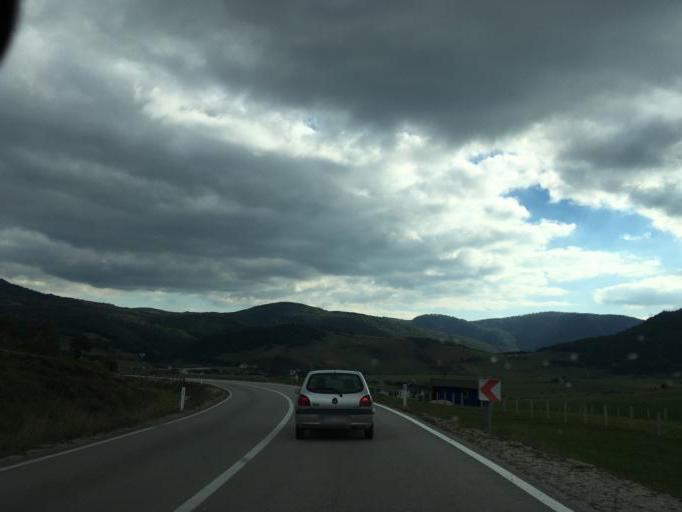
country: BA
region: Federation of Bosnia and Herzegovina
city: Novi Travnik
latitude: 44.1122
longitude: 17.5750
